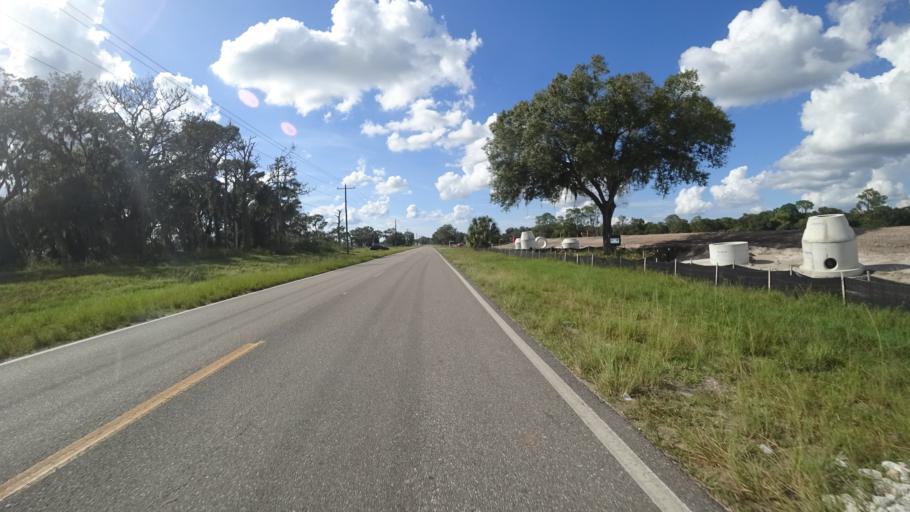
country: US
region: Florida
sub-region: Manatee County
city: Ellenton
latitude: 27.5555
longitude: -82.3957
